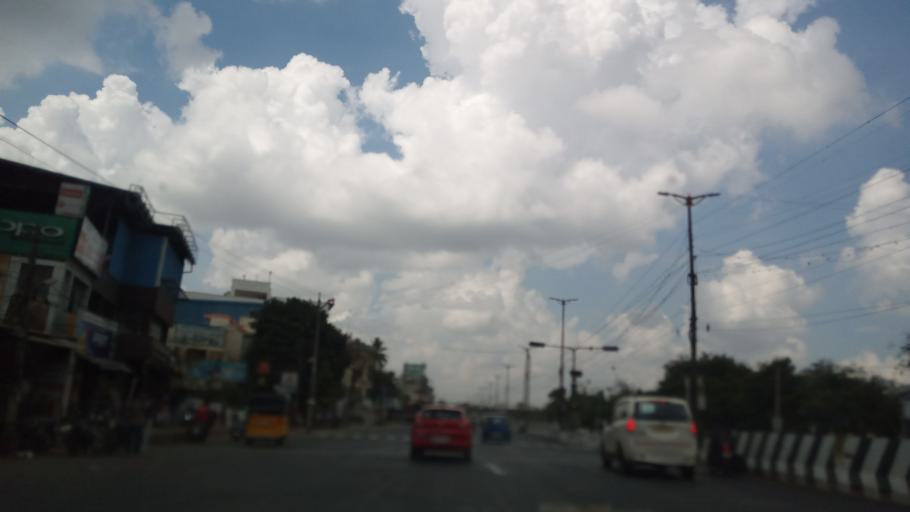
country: IN
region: Tamil Nadu
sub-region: Kancheepuram
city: Pallavaram
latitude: 12.9427
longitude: 80.1334
